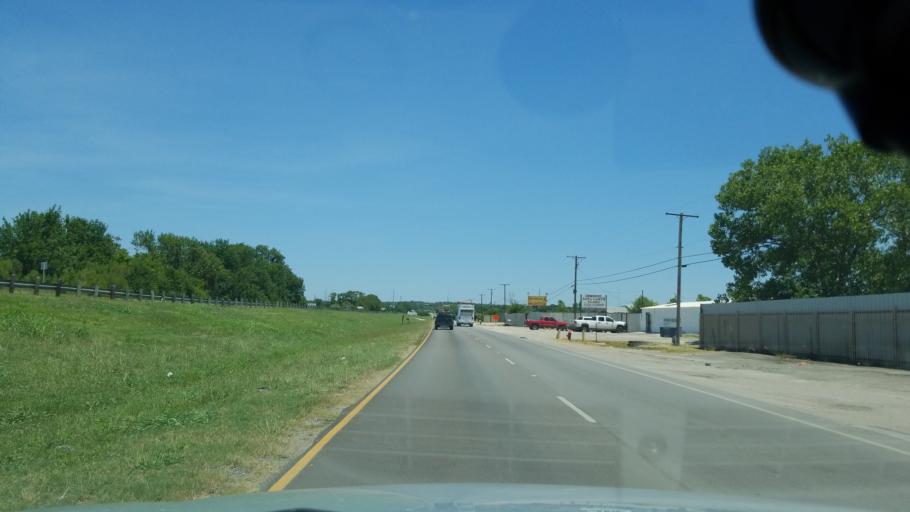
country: US
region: Texas
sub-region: Dallas County
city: Cockrell Hill
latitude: 32.7468
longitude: -96.9366
